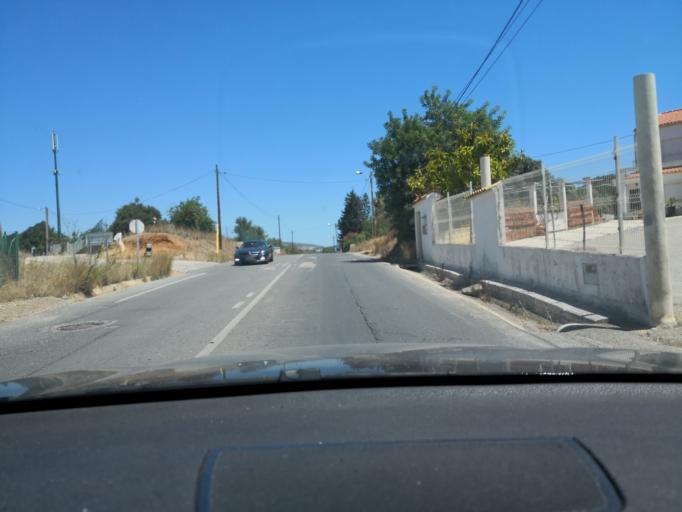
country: PT
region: Faro
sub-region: Loule
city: Boliqueime
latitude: 37.1124
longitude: -8.1547
